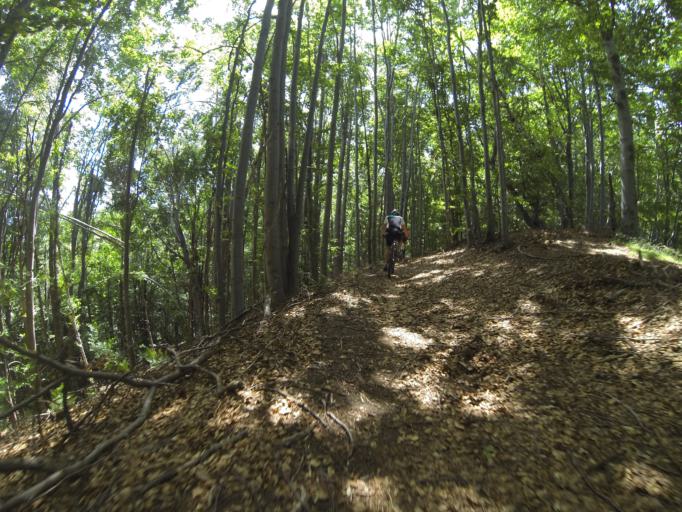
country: RO
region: Valcea
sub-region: Oras Baile Olanesti
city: Cheia
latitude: 45.2295
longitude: 24.1837
